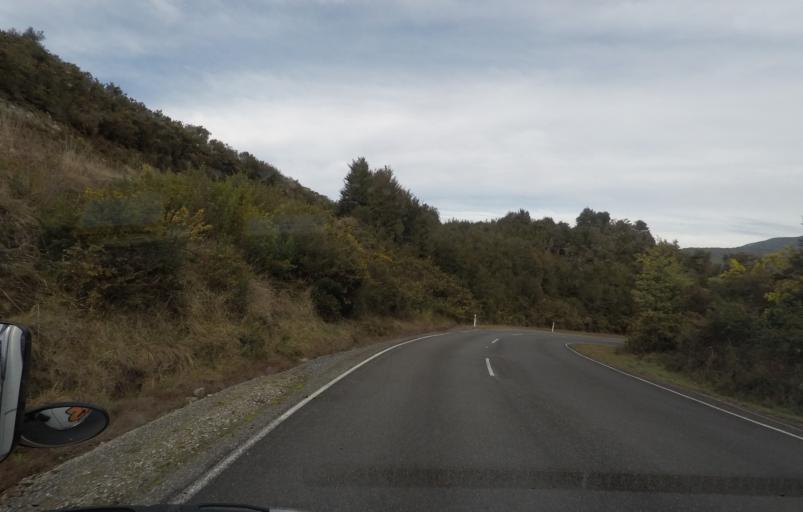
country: NZ
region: Tasman
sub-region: Tasman District
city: Takaka
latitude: -40.8470
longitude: 172.7728
